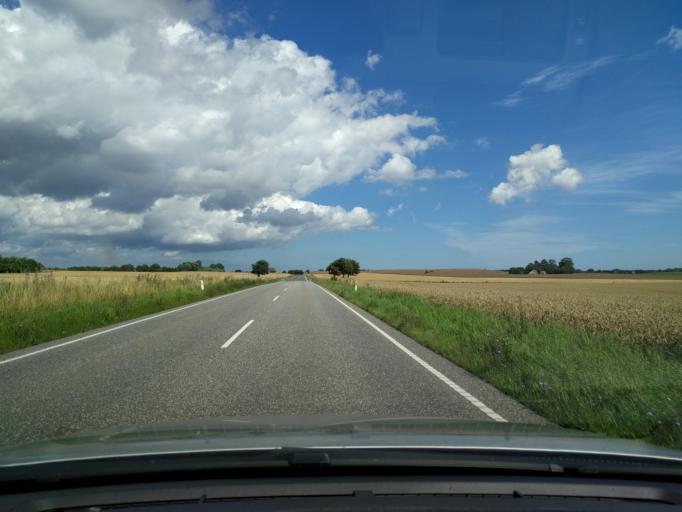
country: DK
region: Zealand
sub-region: Guldborgsund Kommune
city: Stubbekobing
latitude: 54.9112
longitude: 12.1353
